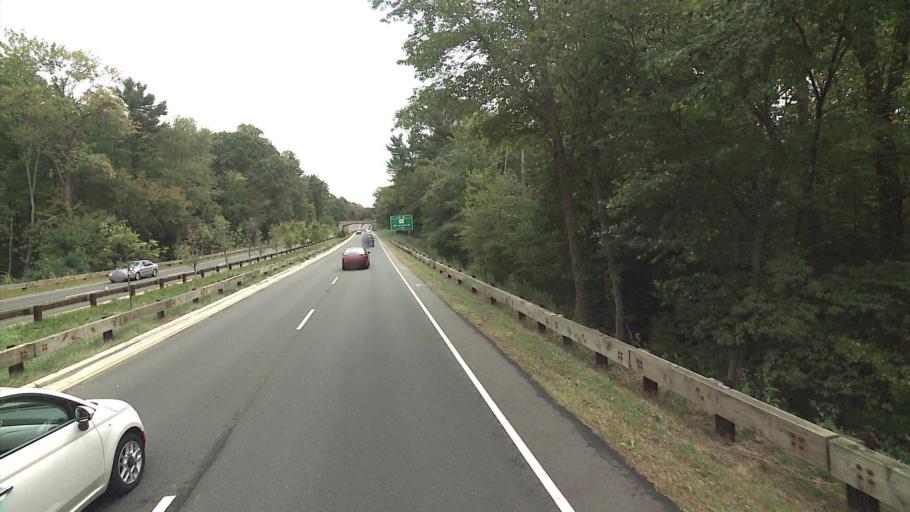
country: US
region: Connecticut
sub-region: Fairfield County
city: North Stamford
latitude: 41.1188
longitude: -73.5212
